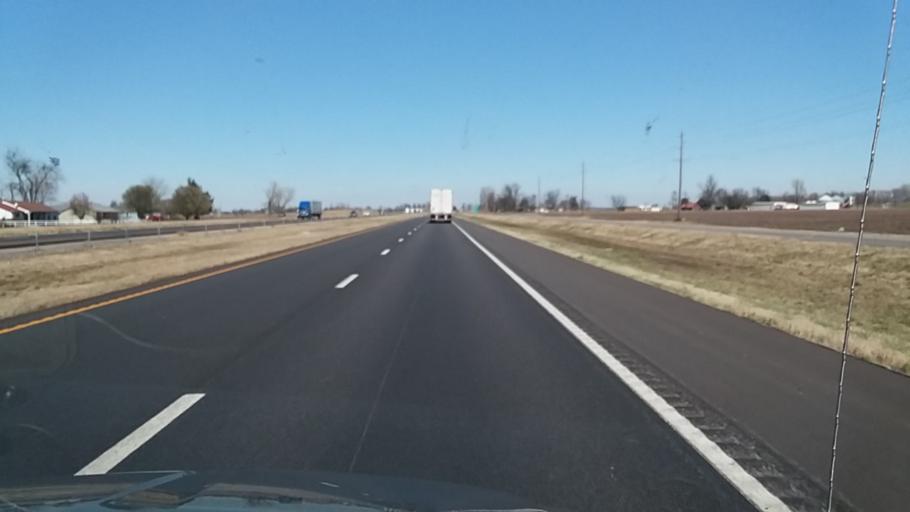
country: US
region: Missouri
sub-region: Pemiscot County
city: Hayti
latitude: 36.2862
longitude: -89.7084
